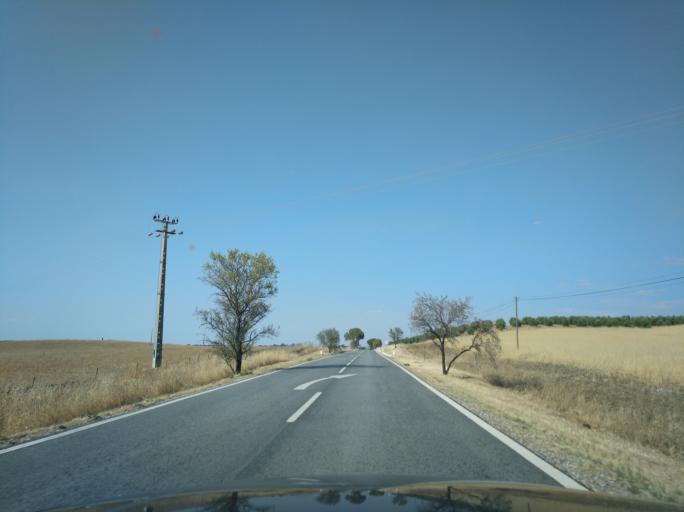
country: ES
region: Andalusia
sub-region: Provincia de Huelva
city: Rosal de la Frontera
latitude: 38.0504
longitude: -7.2572
